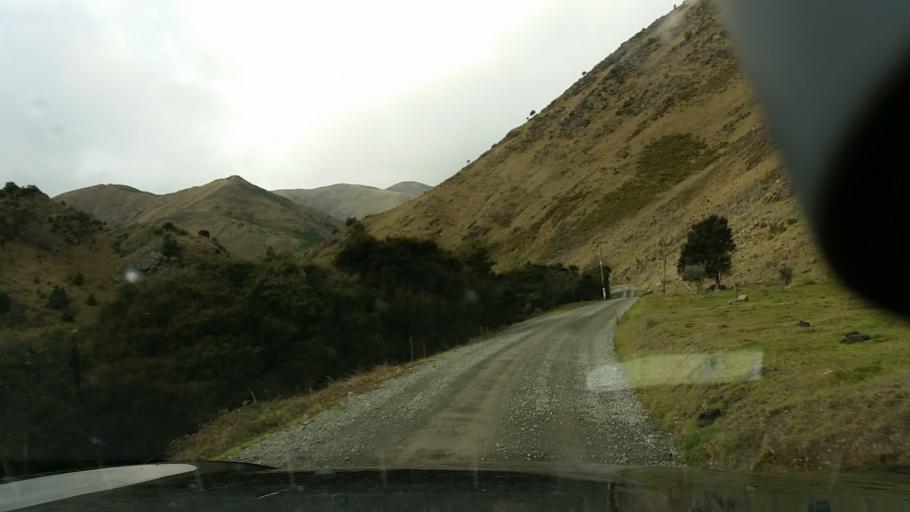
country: NZ
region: Tasman
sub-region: Tasman District
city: Richmond
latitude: -41.7312
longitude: 173.4567
